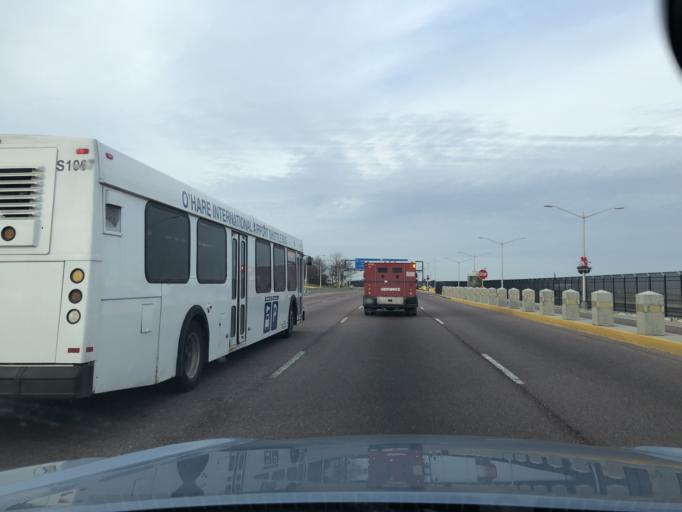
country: US
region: Illinois
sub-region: Cook County
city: Rosemont
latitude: 41.9823
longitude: -87.8995
